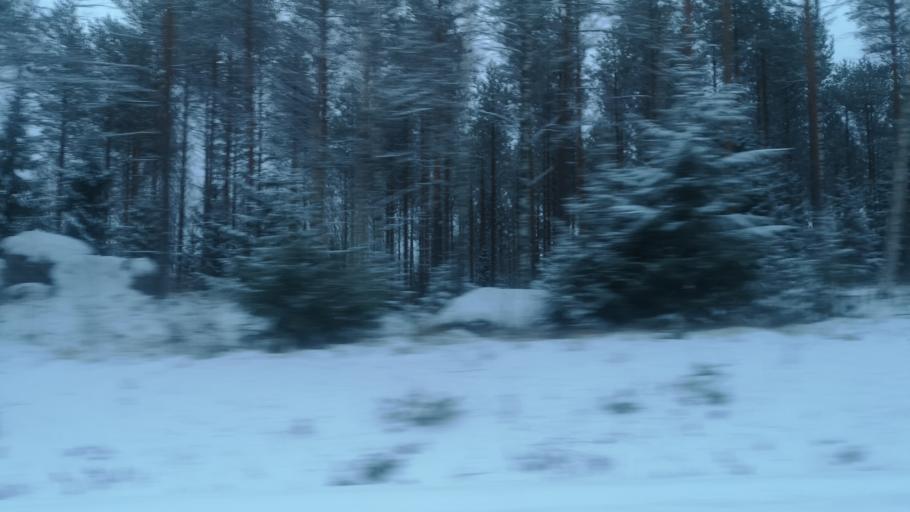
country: FI
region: Southern Savonia
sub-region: Savonlinna
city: Savonlinna
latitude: 62.0183
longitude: 28.7283
